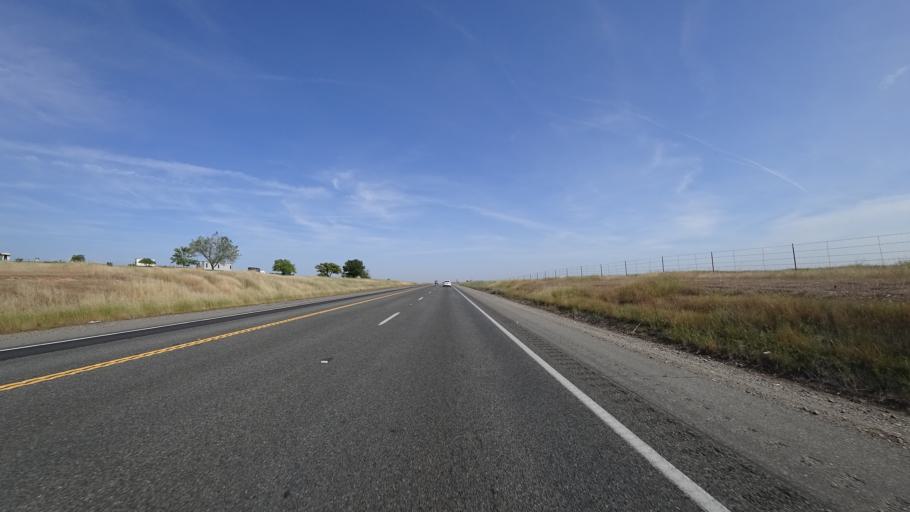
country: US
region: California
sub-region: Tehama County
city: Los Molinos
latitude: 39.9289
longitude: -122.0297
